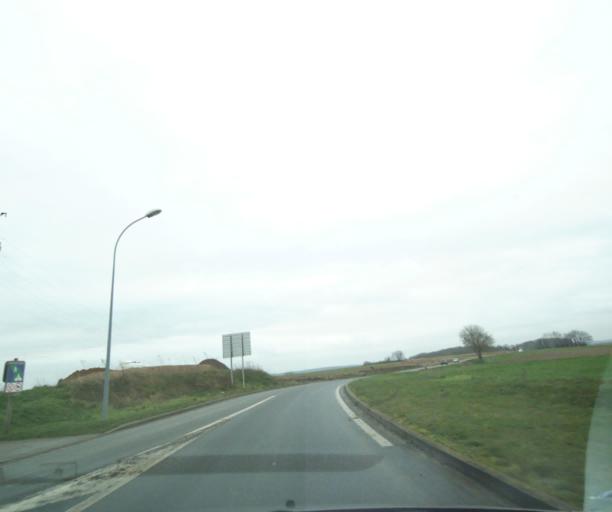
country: FR
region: Picardie
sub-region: Departement de l'Oise
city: Noyon
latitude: 49.5752
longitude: 2.9705
